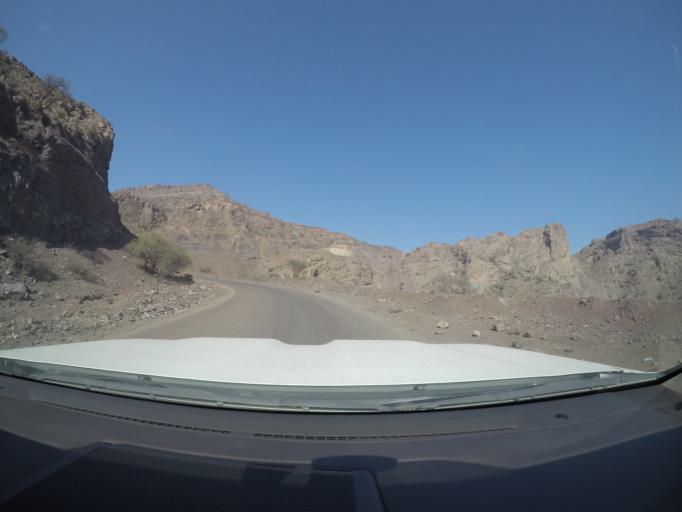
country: YE
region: Ad Dali'
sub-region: Ad Dhale'e
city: Dhalie
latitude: 13.6701
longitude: 44.7705
